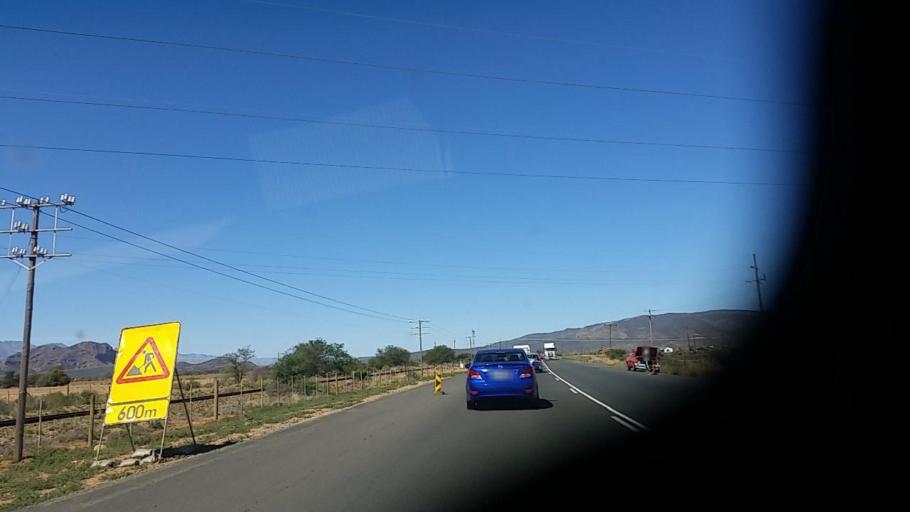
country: ZA
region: Western Cape
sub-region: Eden District Municipality
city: Oudtshoorn
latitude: -33.5608
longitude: 22.3876
